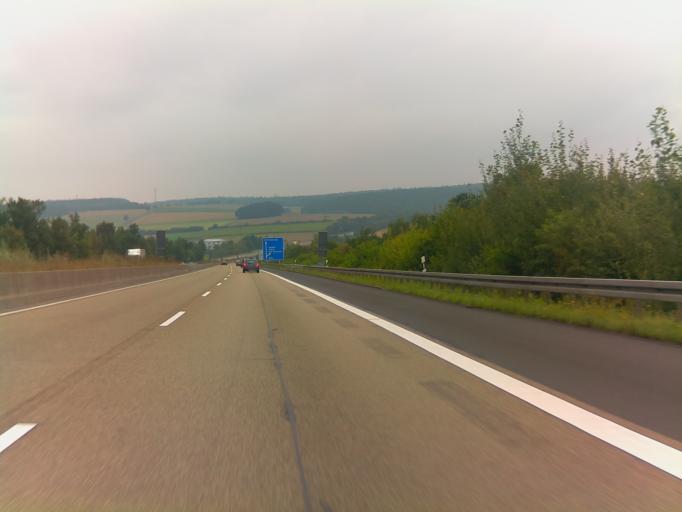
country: DE
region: Hesse
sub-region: Regierungsbezirk Kassel
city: Burghaun
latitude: 50.6515
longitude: 9.6814
